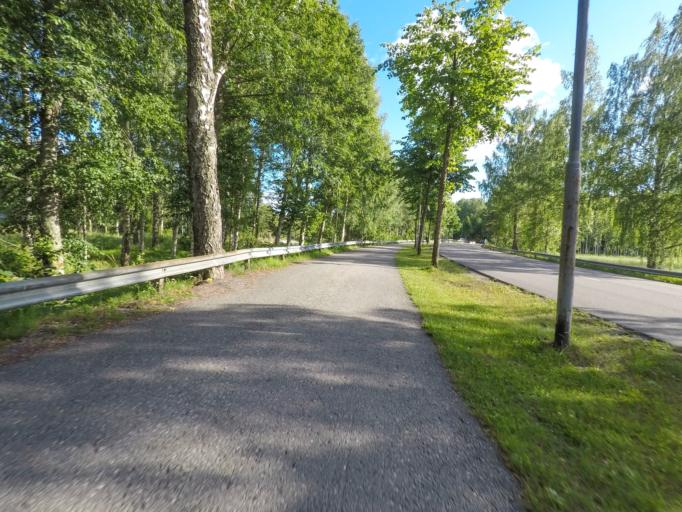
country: FI
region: South Karelia
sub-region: Lappeenranta
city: Lappeenranta
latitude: 61.0754
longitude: 28.1512
